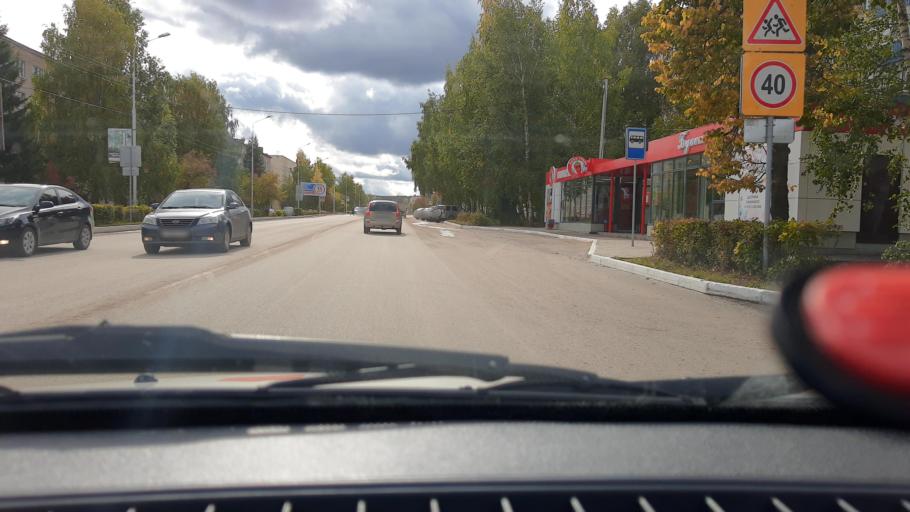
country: RU
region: Bashkortostan
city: Belebey
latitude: 54.1008
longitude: 54.1075
